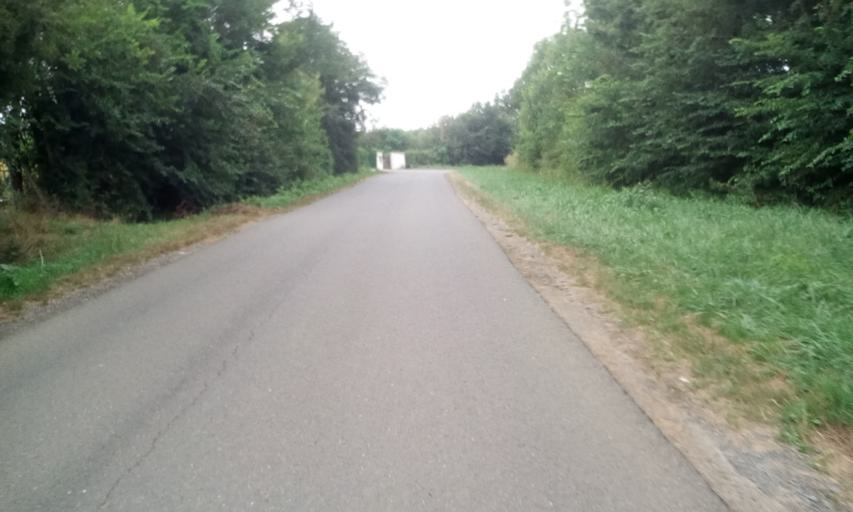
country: FR
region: Lower Normandy
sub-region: Departement du Calvados
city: Sannerville
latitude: 49.1954
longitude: -0.2235
